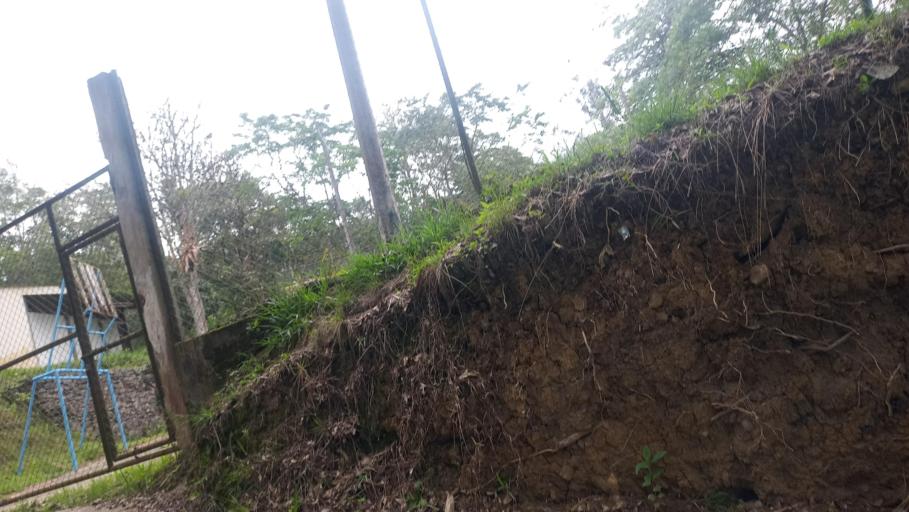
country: CO
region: Boyaca
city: Guateque
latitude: 5.0113
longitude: -73.4895
